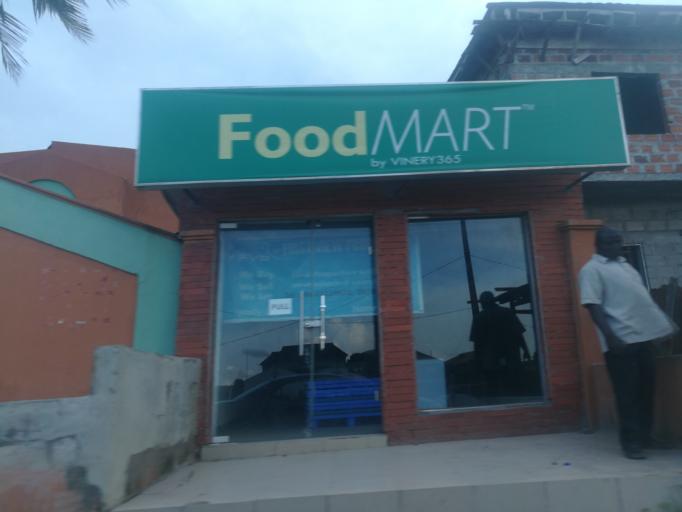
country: NG
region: Lagos
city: Somolu
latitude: 6.5544
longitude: 3.3851
